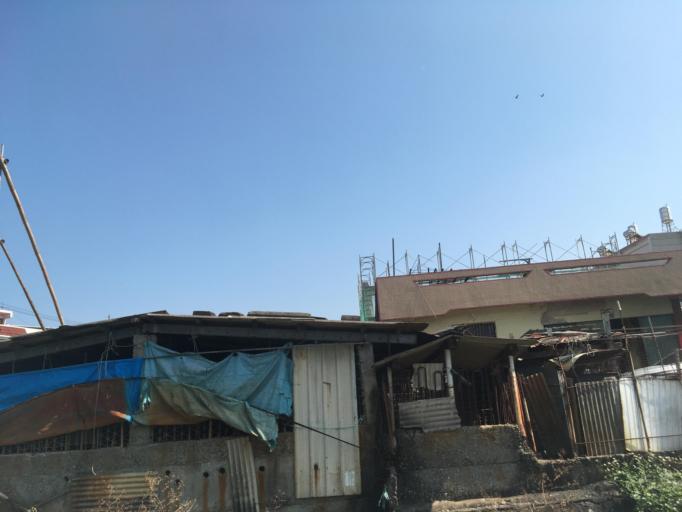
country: TW
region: Taiwan
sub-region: Chiayi
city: Jiayi Shi
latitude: 23.5534
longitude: 120.4132
